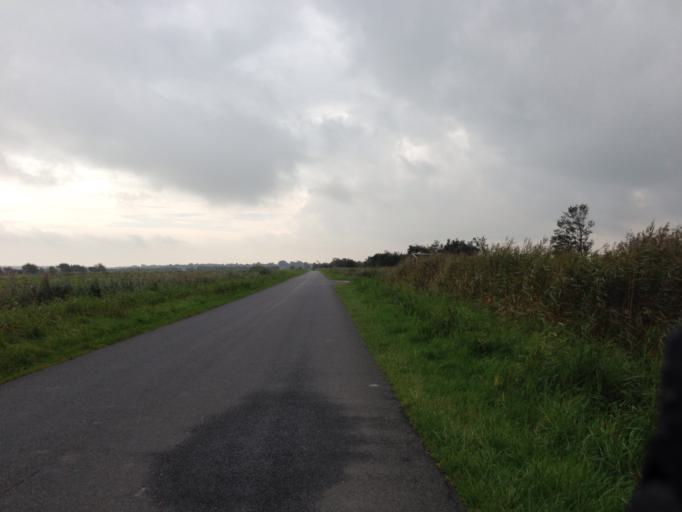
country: DE
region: Schleswig-Holstein
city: Oevenum
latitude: 54.7238
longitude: 8.5425
